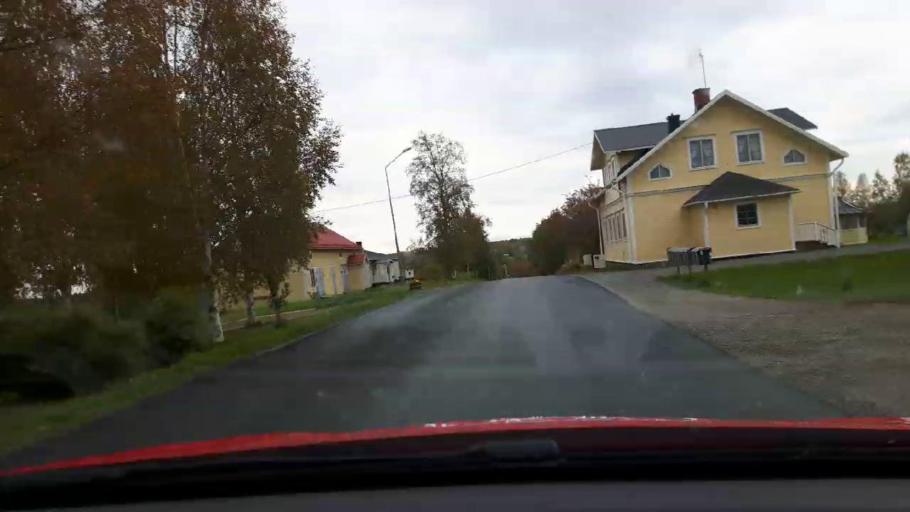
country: SE
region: Jaemtland
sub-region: Bergs Kommun
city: Hoverberg
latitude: 62.9181
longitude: 14.5203
